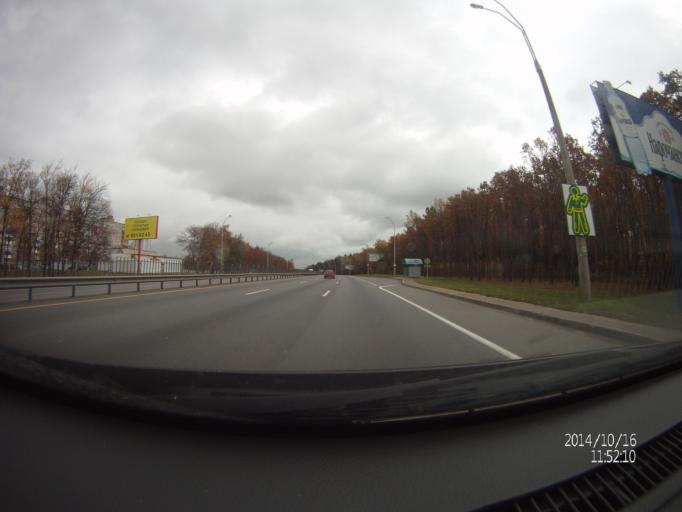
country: BY
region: Minsk
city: Hatava
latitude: 53.8335
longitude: 27.6392
